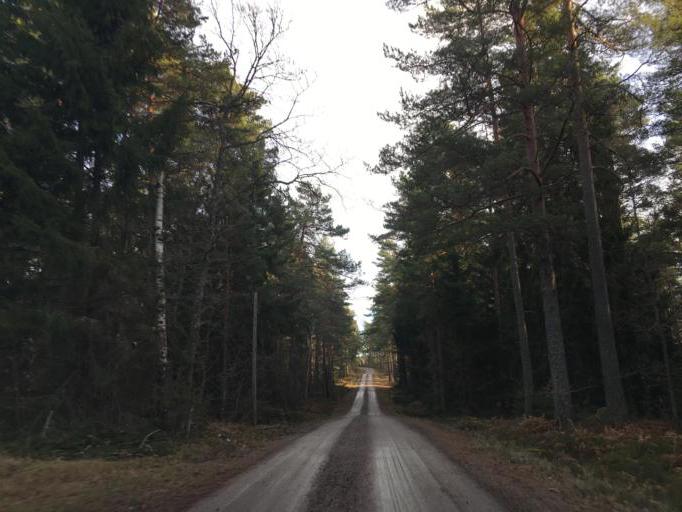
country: SE
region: Kalmar
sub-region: Vasterviks Kommun
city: Vaestervik
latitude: 57.6230
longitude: 16.5534
